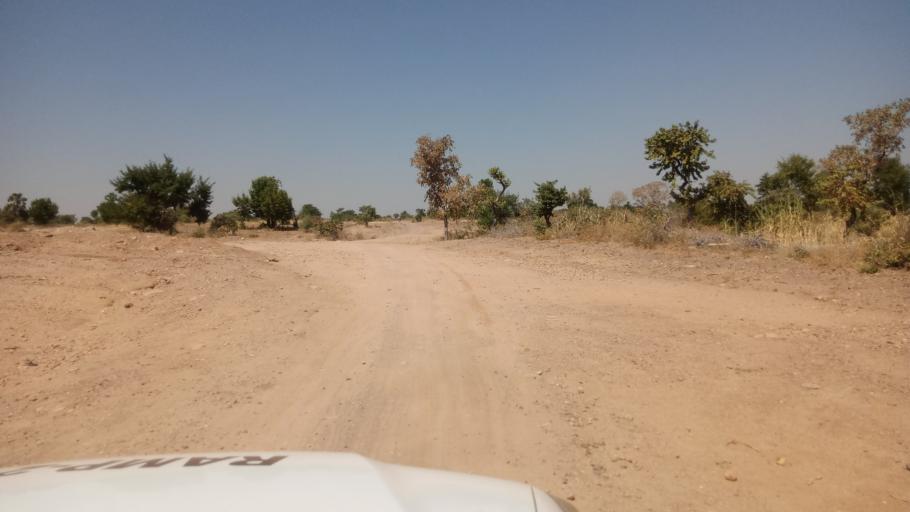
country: NG
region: Adamawa
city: Mayo Belwa
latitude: 9.0945
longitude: 12.0236
